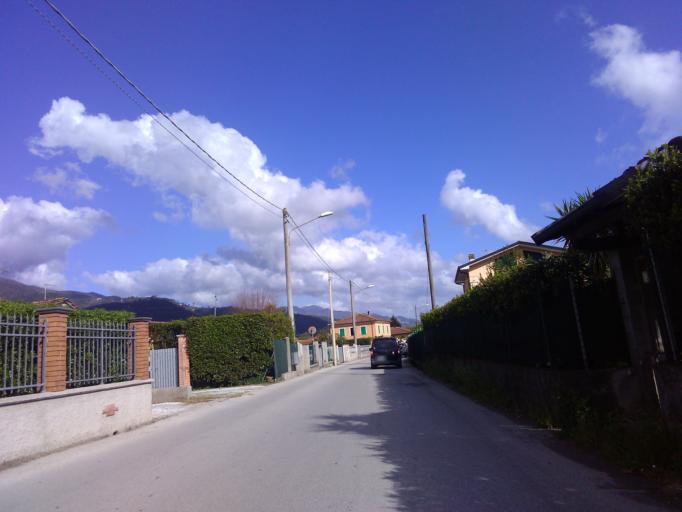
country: IT
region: Tuscany
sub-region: Provincia di Massa-Carrara
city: Capanne-Prato-Cinquale
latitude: 44.0104
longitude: 10.1434
